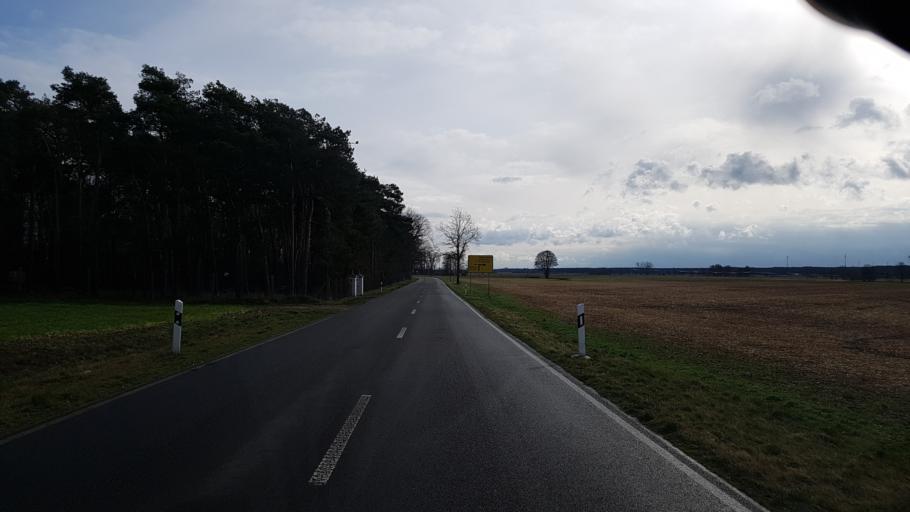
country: DE
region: Brandenburg
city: Schlieben
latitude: 51.7142
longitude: 13.4047
